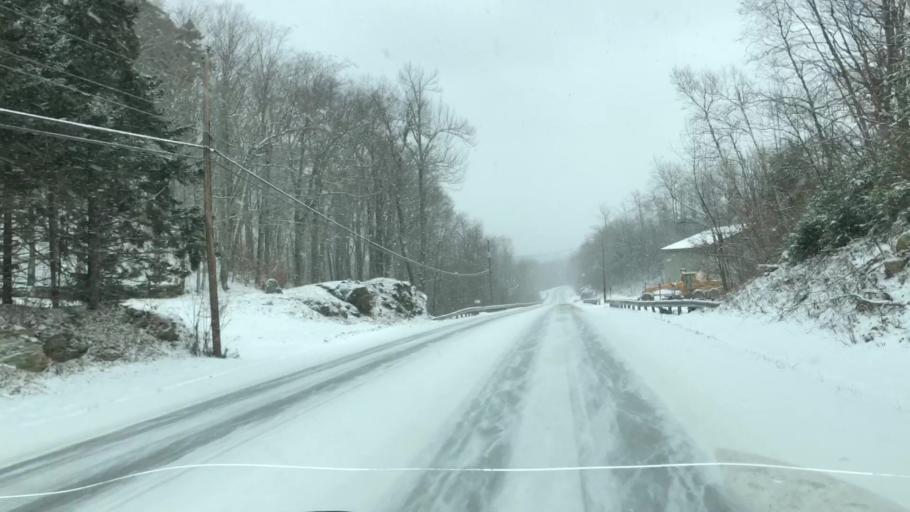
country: US
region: Massachusetts
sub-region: Berkshire County
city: Adams
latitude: 42.5807
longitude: -73.0619
